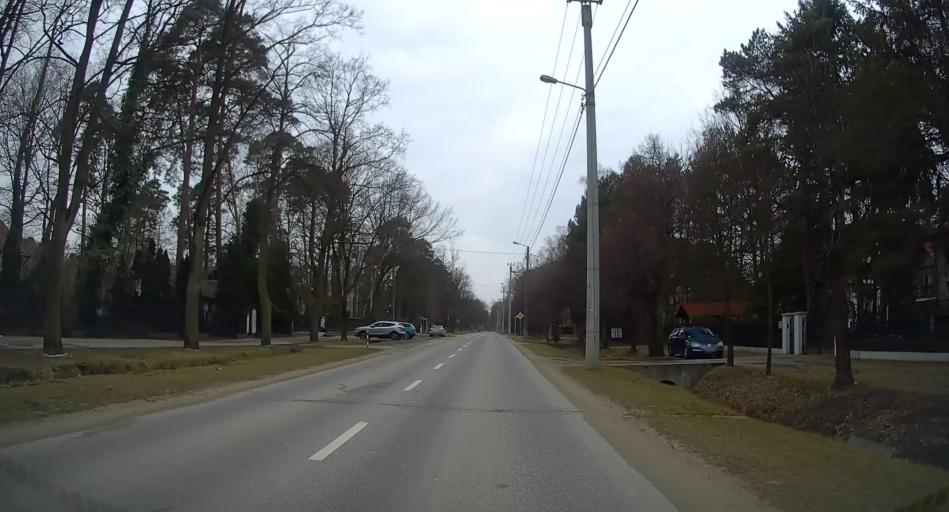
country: PL
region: Masovian Voivodeship
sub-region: Powiat piaseczynski
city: Piaseczno
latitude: 52.0610
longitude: 21.0070
